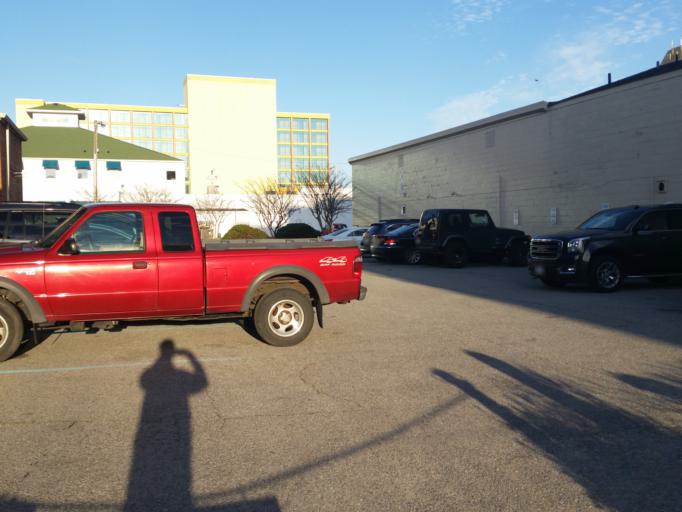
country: US
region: Virginia
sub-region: City of Virginia Beach
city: Virginia Beach
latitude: 36.8530
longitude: -75.9775
